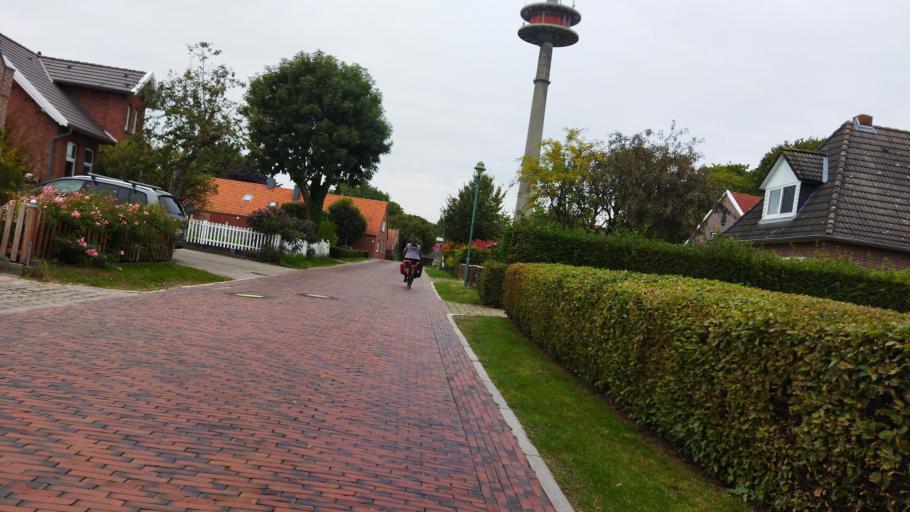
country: DE
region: Lower Saxony
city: Leer
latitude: 53.2617
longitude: 7.4353
